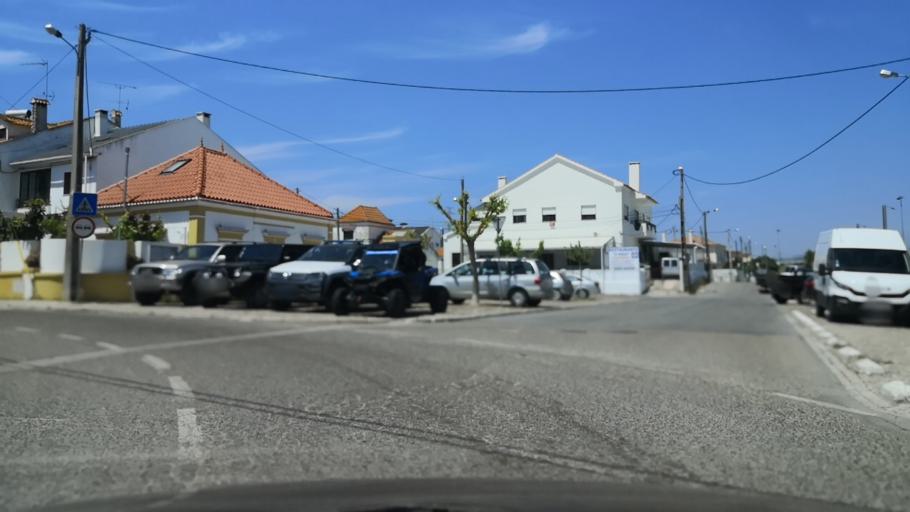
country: PT
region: Setubal
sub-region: Palmela
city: Palmela
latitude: 38.5770
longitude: -8.8742
